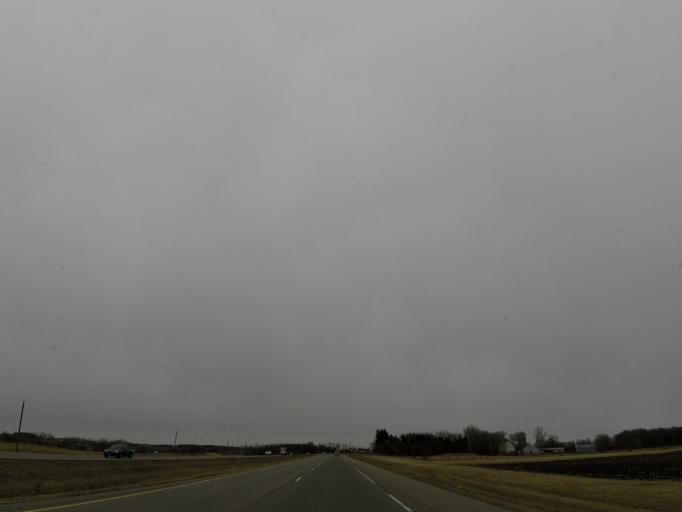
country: US
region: Minnesota
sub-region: Le Sueur County
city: Le Sueur
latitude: 44.5135
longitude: -93.8514
